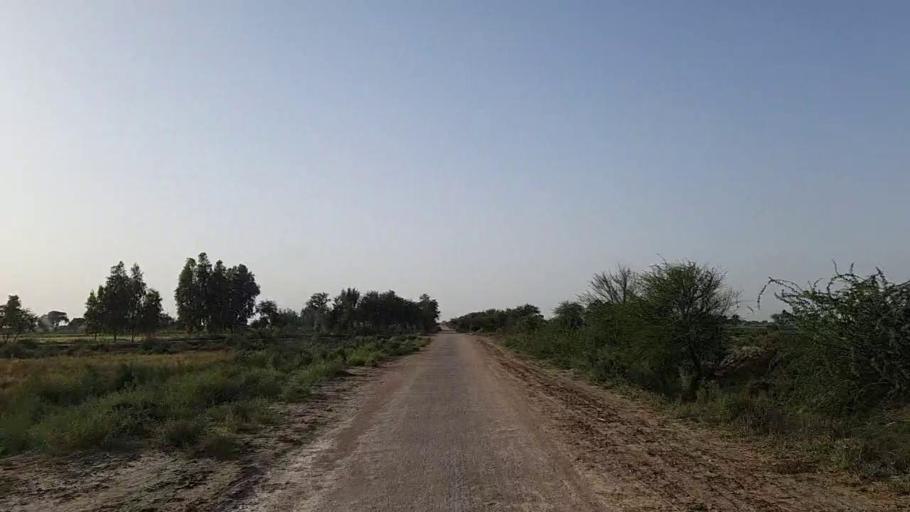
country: PK
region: Sindh
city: Jati
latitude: 24.3275
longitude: 68.1619
